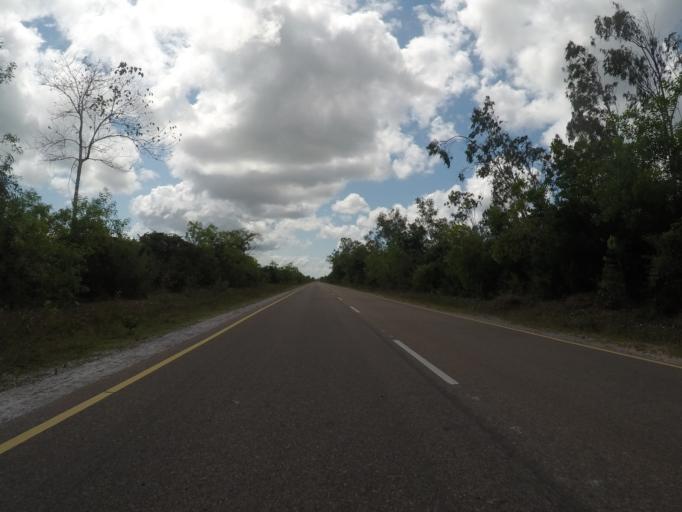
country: TZ
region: Zanzibar Central/South
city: Koani
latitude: -6.2583
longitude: 39.3580
